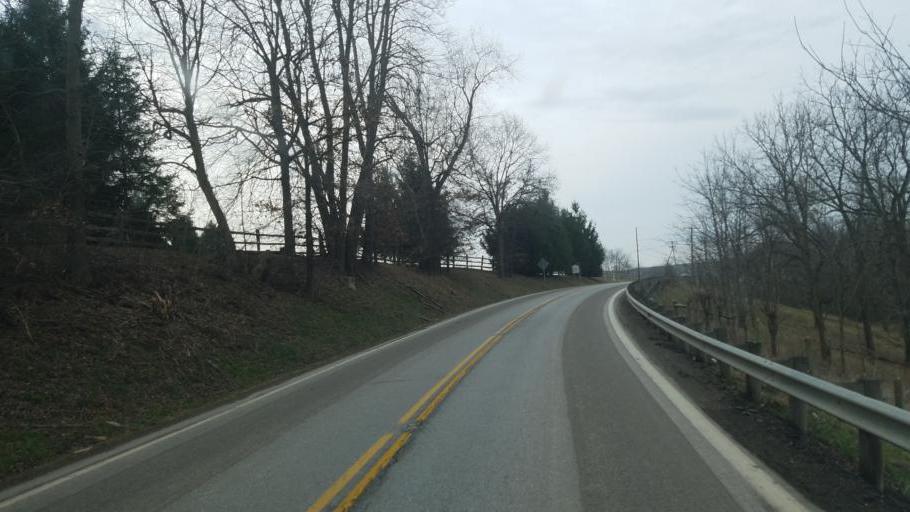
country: US
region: Ohio
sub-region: Holmes County
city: Millersburg
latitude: 40.5238
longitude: -81.8043
